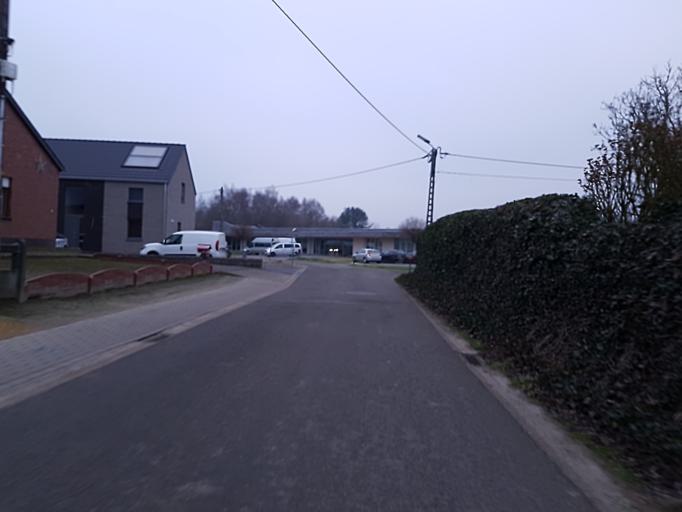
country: BE
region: Flanders
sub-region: Provincie Vlaams-Brabant
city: Haacht
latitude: 50.9830
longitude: 4.6331
